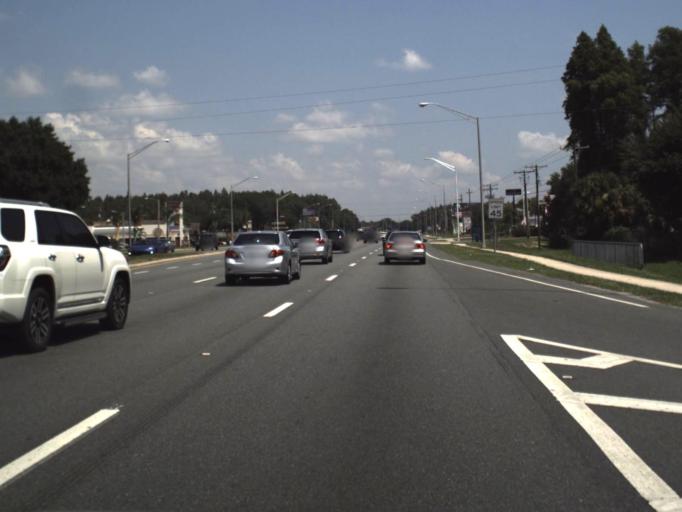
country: US
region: Florida
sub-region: Hillsborough County
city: Carrollwood
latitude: 28.0523
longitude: -82.5040
